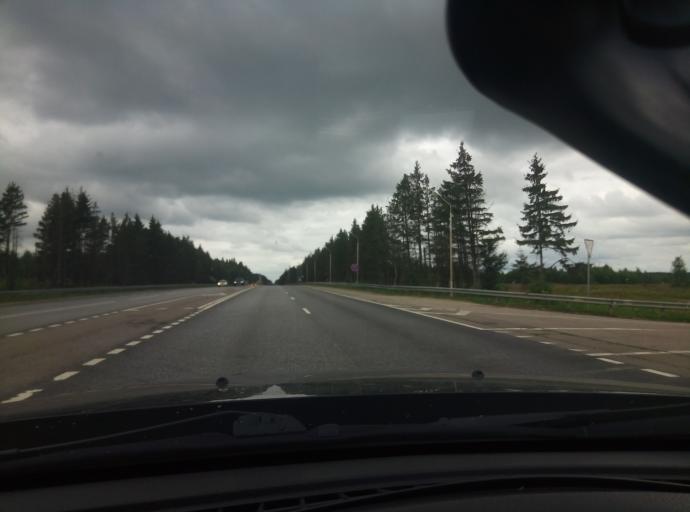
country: RU
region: Kaluga
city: Maloyaroslavets
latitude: 55.0077
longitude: 36.5400
